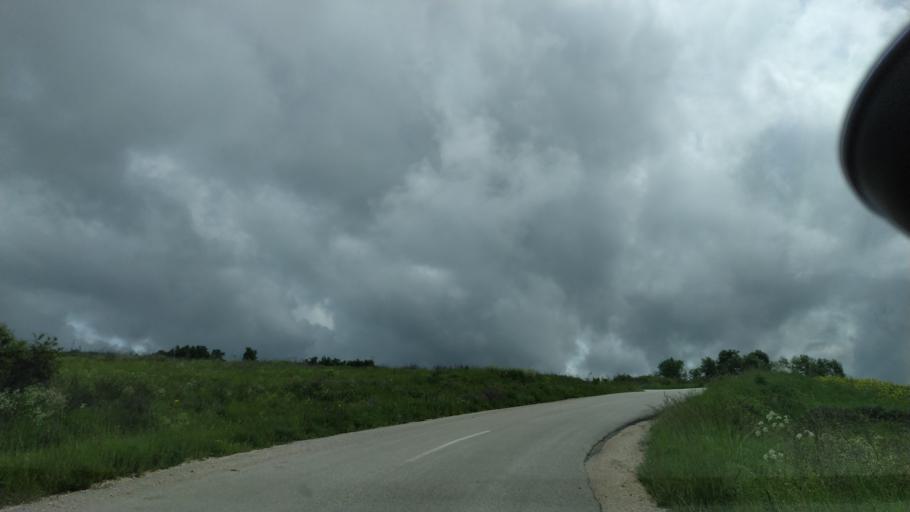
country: RS
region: Central Serbia
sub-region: Zajecarski Okrug
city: Soko Banja
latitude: 43.6942
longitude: 21.9356
